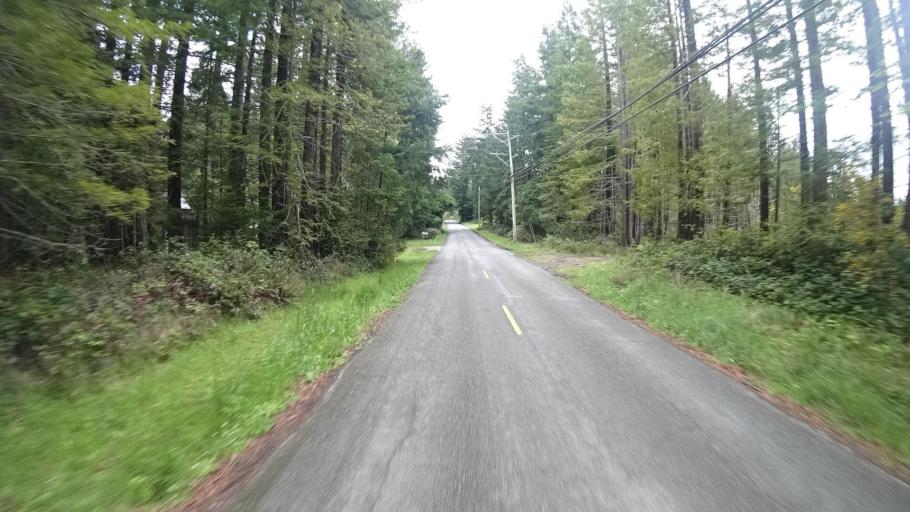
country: US
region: California
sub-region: Humboldt County
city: Bayside
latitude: 40.7914
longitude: -124.0210
